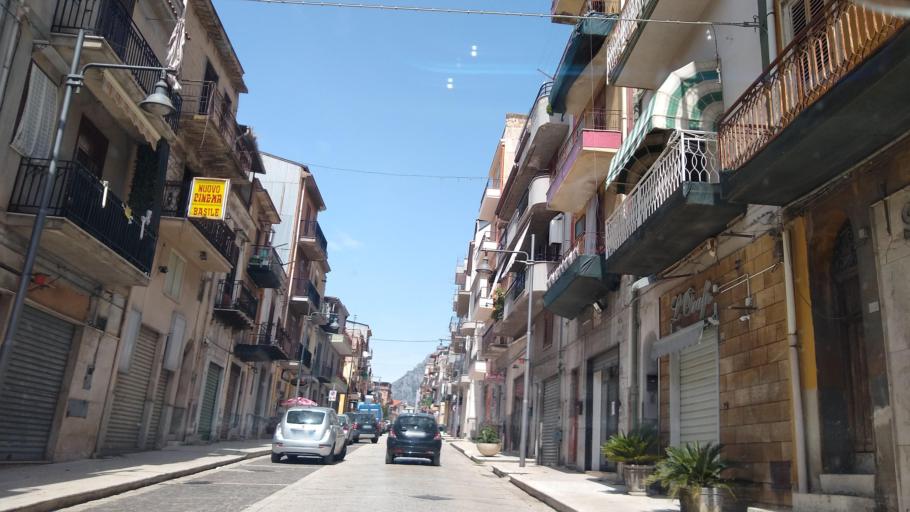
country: IT
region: Sicily
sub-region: Palermo
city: San Giuseppe Jato
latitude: 37.9692
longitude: 13.1821
